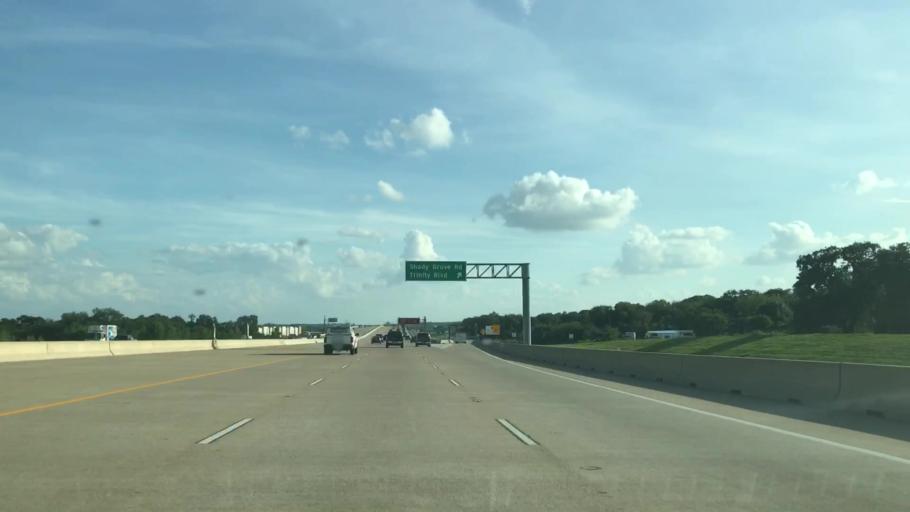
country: US
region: Texas
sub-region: Dallas County
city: Grand Prairie
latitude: 32.8095
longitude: -97.0185
